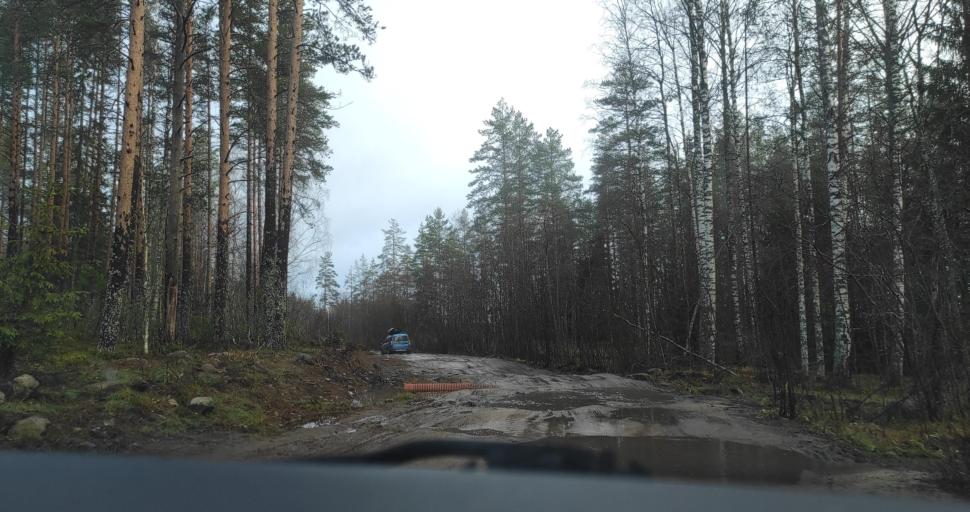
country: RU
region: Republic of Karelia
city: Pitkyaranta
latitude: 61.7394
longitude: 31.3907
